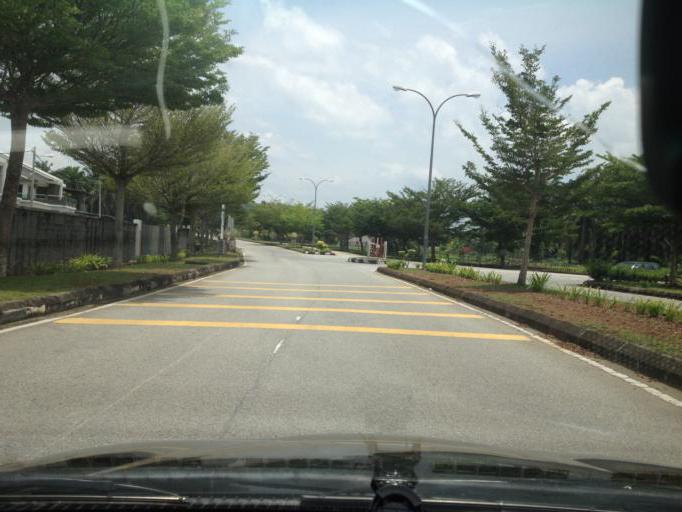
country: MY
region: Kedah
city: Sungai Petani
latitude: 5.6062
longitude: 100.5459
